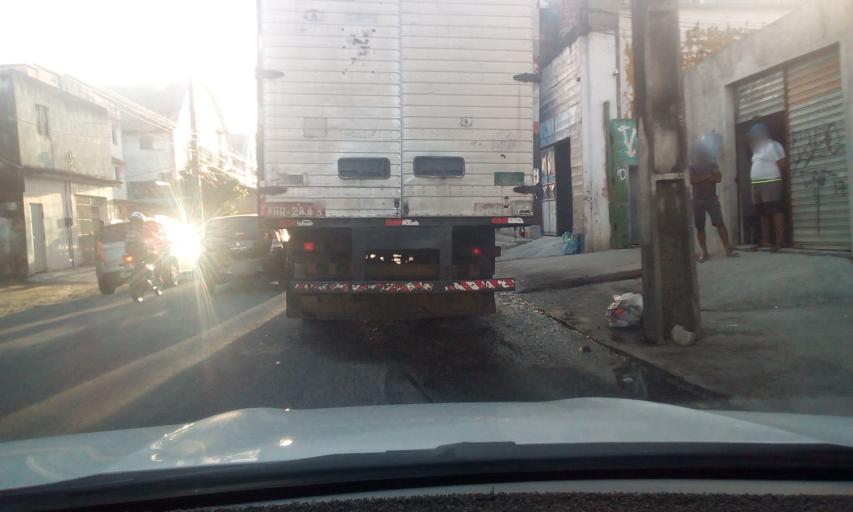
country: BR
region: Pernambuco
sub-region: Recife
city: Recife
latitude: -8.0771
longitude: -34.8981
